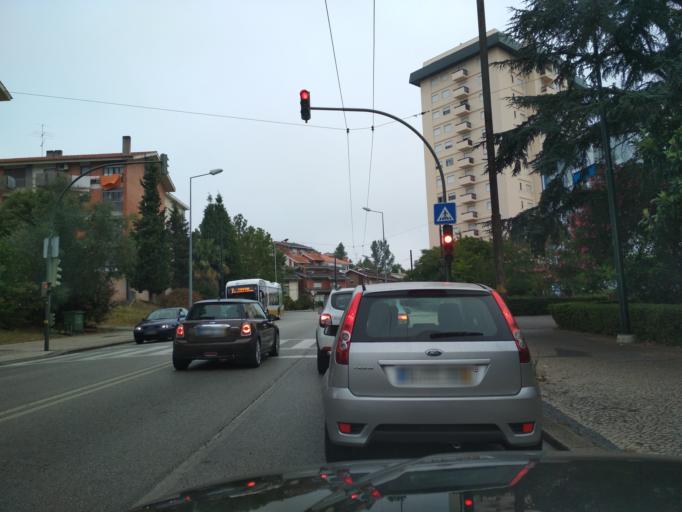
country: PT
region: Coimbra
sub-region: Coimbra
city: Coimbra
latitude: 40.2065
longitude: -8.4041
